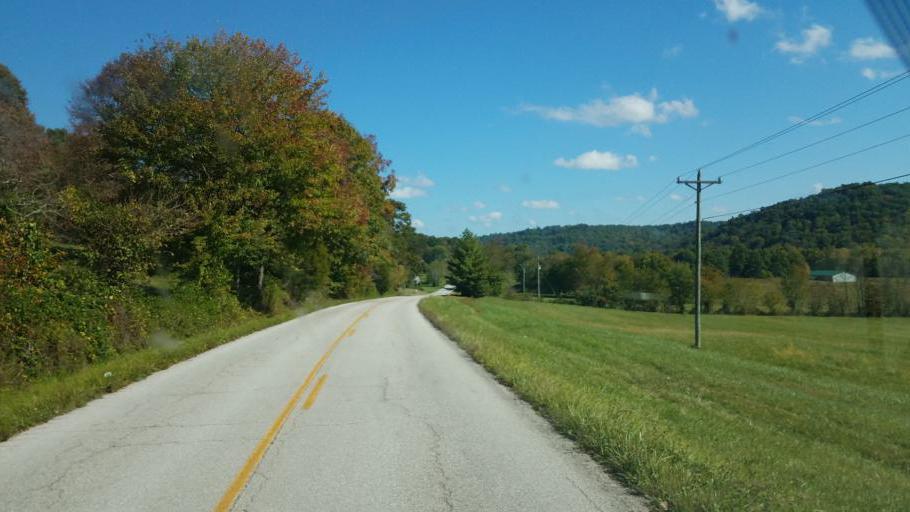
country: US
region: Kentucky
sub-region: Fleming County
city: Flemingsburg
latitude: 38.4687
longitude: -83.5548
